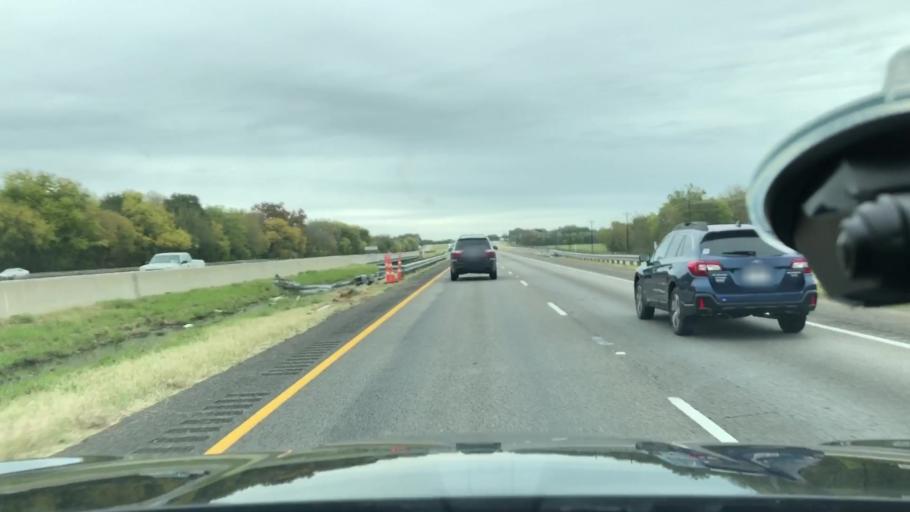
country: US
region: Texas
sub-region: Hopkins County
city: Sulphur Springs
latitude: 33.1495
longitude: -95.4435
